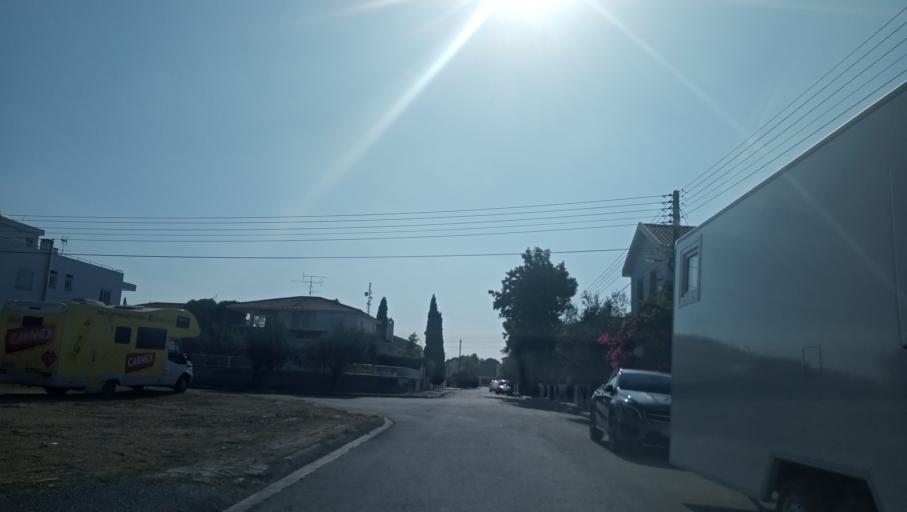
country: CY
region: Lefkosia
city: Nicosia
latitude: 35.1510
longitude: 33.3795
